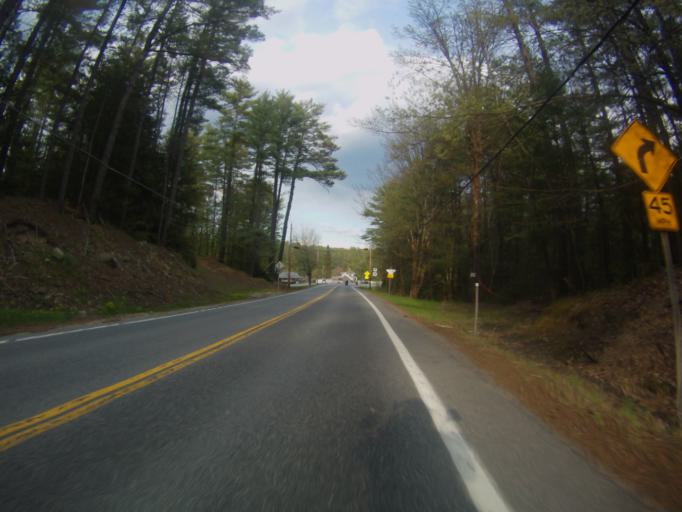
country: US
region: New York
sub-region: Warren County
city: Warrensburg
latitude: 43.6625
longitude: -73.8445
